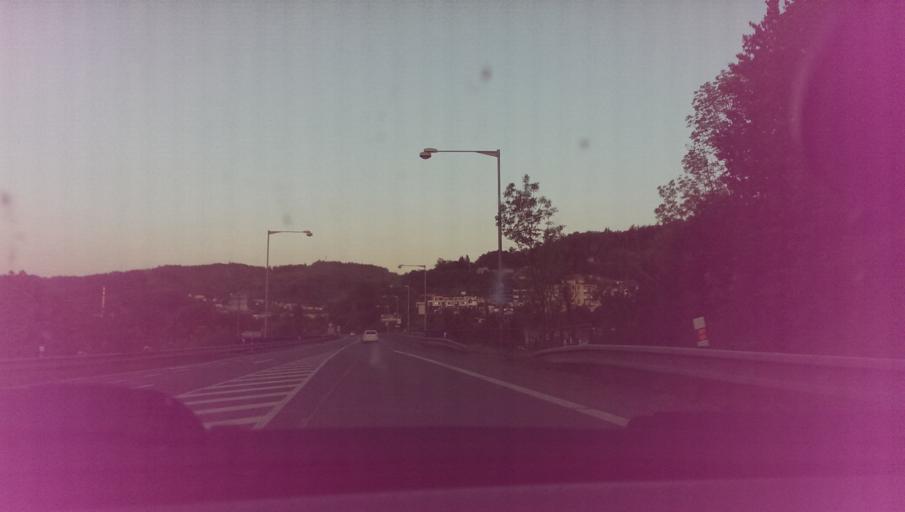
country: CZ
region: Zlin
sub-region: Okres Vsetin
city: Vsetin
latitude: 49.3340
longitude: 17.9865
